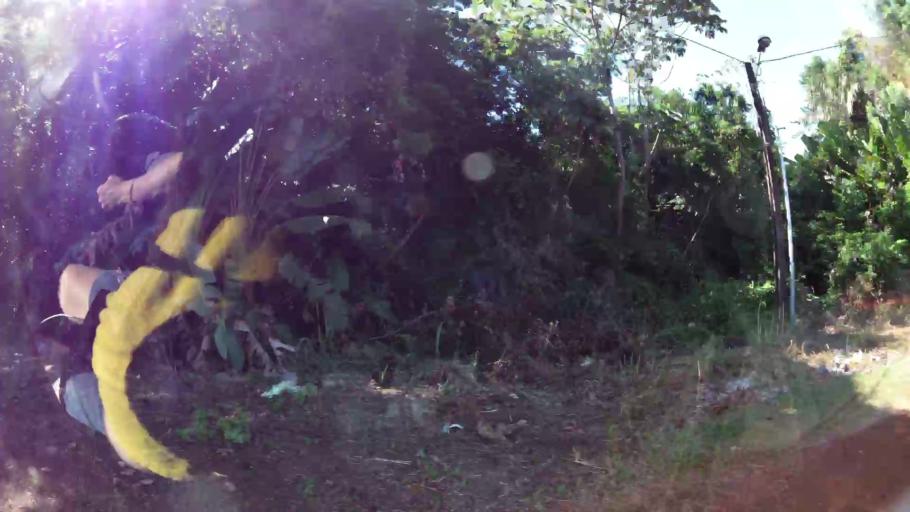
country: GF
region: Guyane
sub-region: Guyane
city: Remire-Montjoly
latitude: 4.9183
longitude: -52.2722
